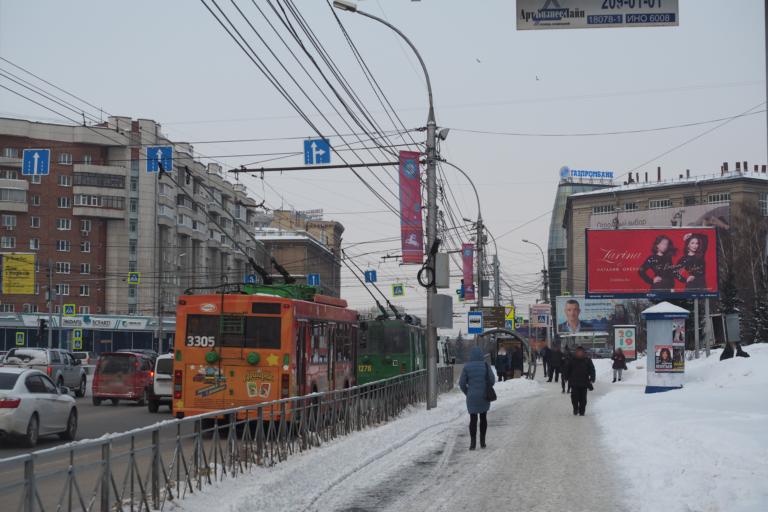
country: RU
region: Novosibirsk
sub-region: Novosibirskiy Rayon
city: Novosibirsk
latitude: 55.0246
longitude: 82.9281
